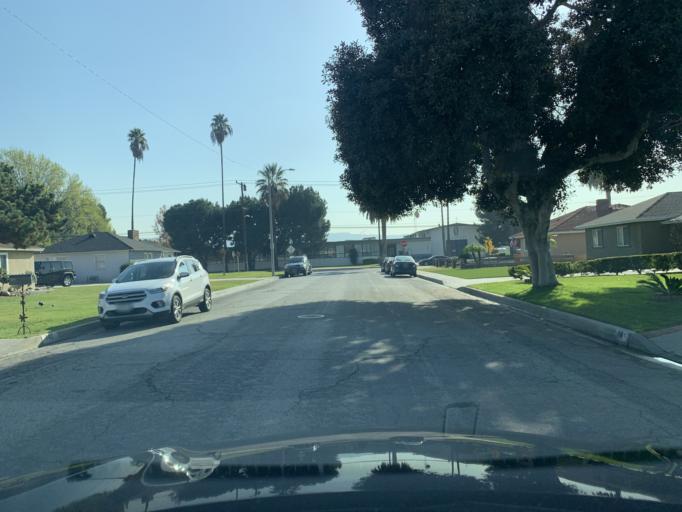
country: US
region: California
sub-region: Los Angeles County
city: Covina
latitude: 34.0761
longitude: -117.8962
